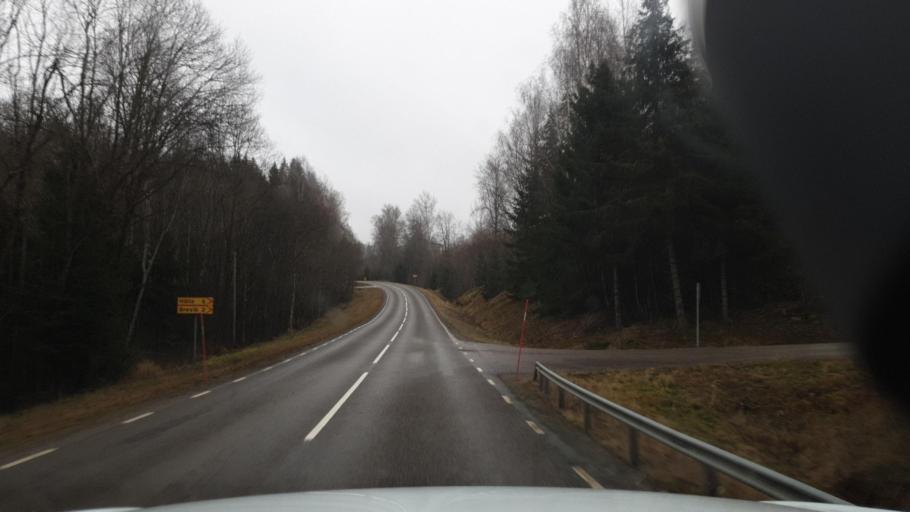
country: SE
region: Vaermland
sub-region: Eda Kommun
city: Amotfors
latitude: 59.7392
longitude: 12.3822
